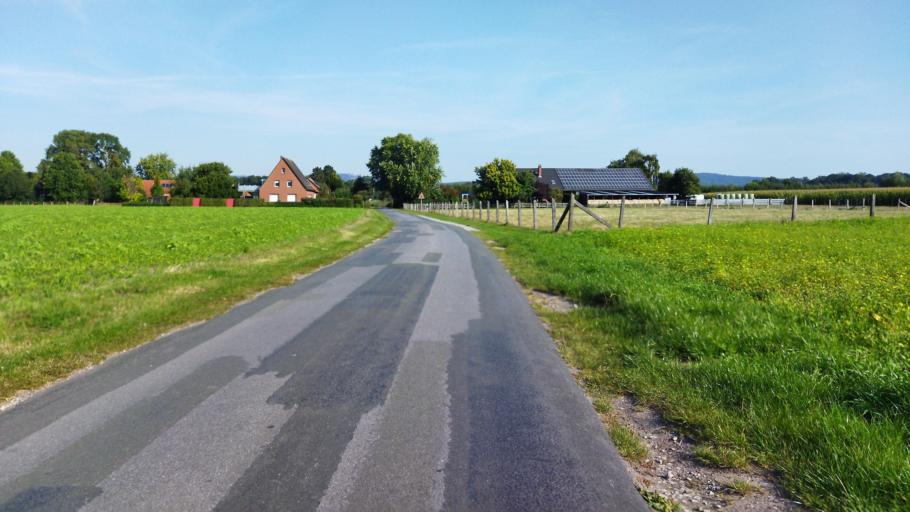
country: DE
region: Lower Saxony
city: Bad Laer
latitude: 52.1122
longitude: 8.0764
